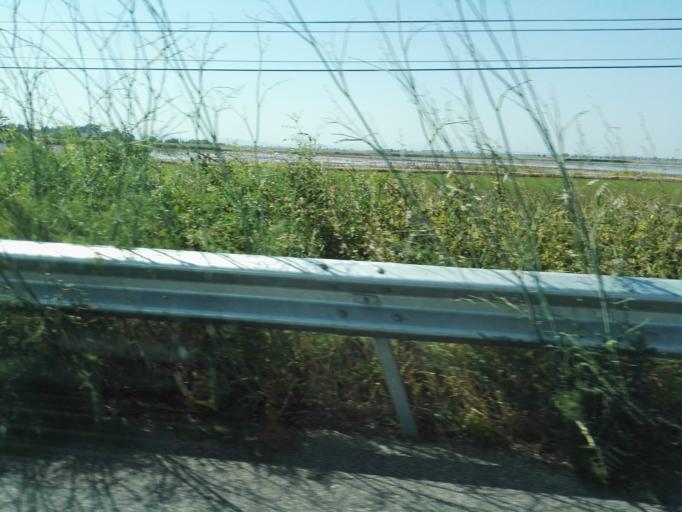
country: PT
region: Santarem
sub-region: Benavente
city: Samora Correia
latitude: 38.9395
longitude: -8.8424
